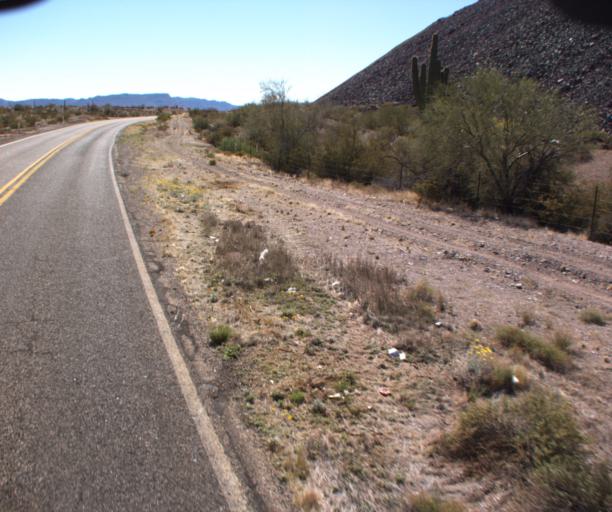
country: US
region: Arizona
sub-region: Pima County
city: Ajo
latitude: 32.3677
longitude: -112.8423
